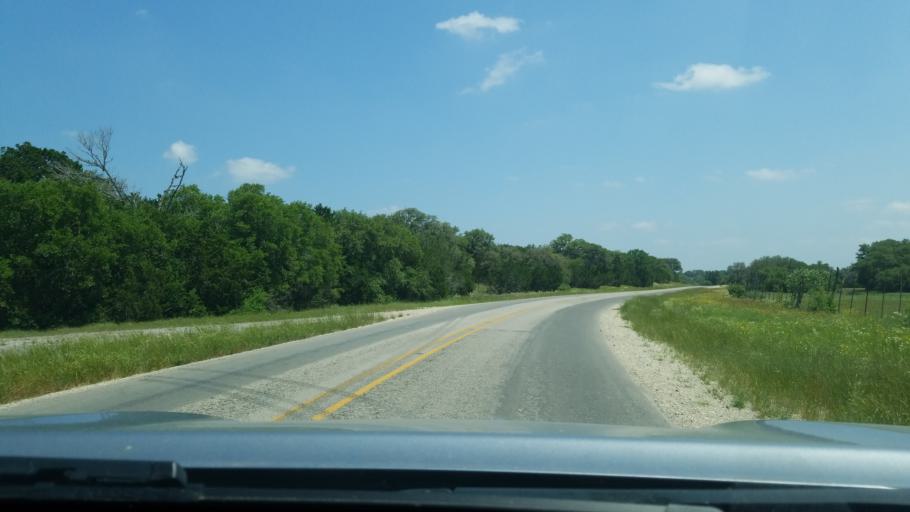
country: US
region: Texas
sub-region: Blanco County
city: Blanco
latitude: 29.9824
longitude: -98.5495
